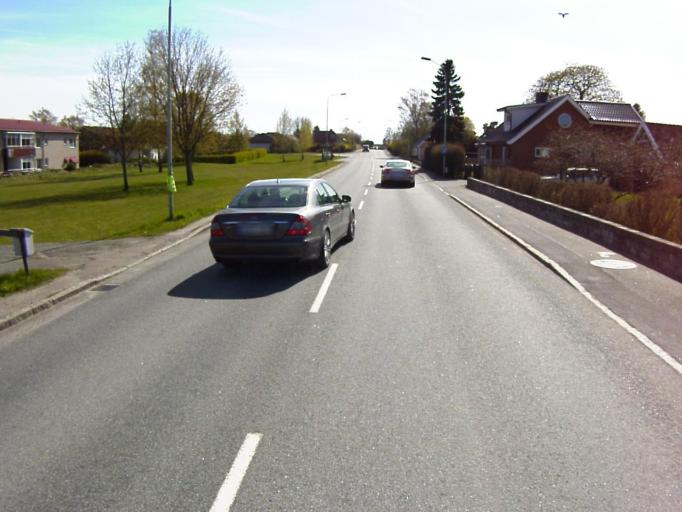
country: SE
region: Skane
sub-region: Kristianstads Kommun
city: Norra Asum
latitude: 56.0001
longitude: 14.0907
